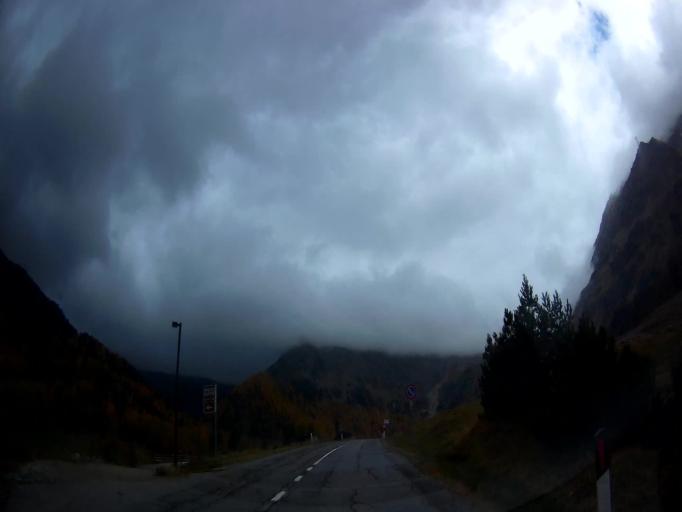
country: IT
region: Trentino-Alto Adige
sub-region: Bolzano
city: Silandro
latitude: 46.7530
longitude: 10.7850
